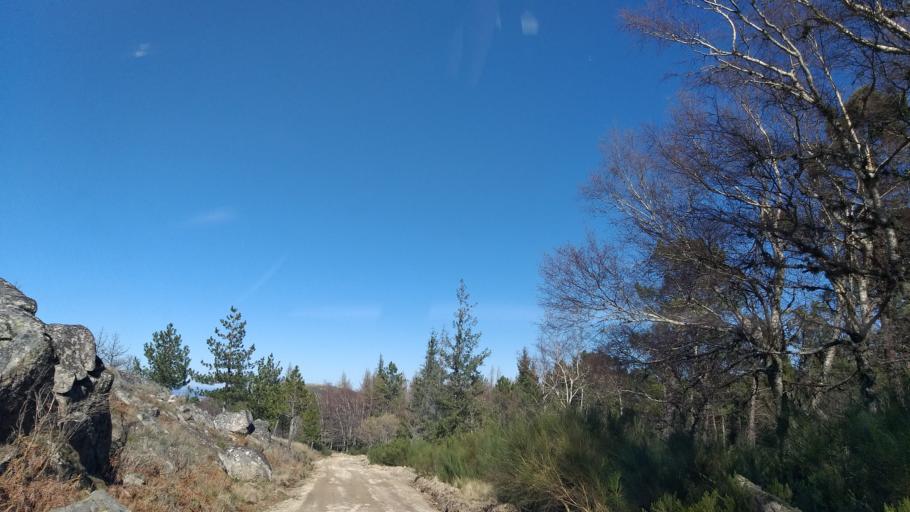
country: PT
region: Guarda
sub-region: Manteigas
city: Manteigas
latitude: 40.4928
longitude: -7.4934
